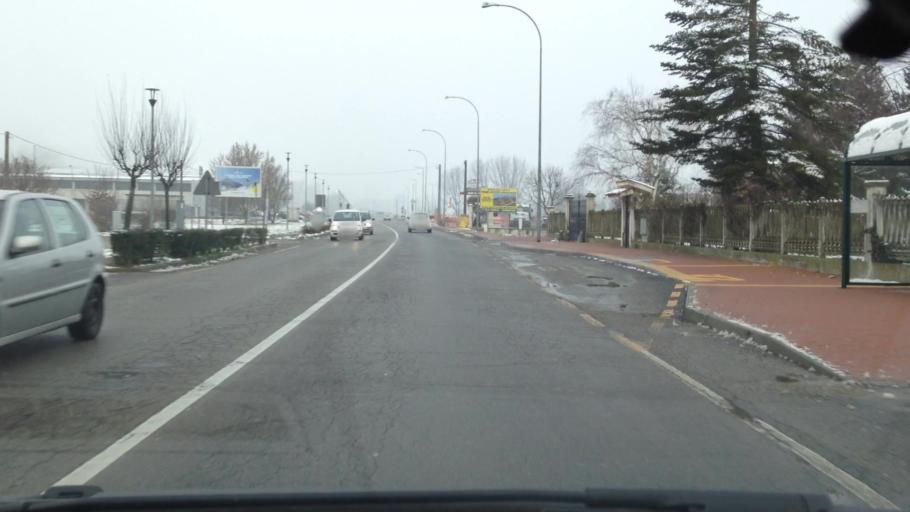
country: IT
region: Piedmont
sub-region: Provincia di Asti
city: Montegrosso
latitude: 44.8198
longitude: 8.2330
